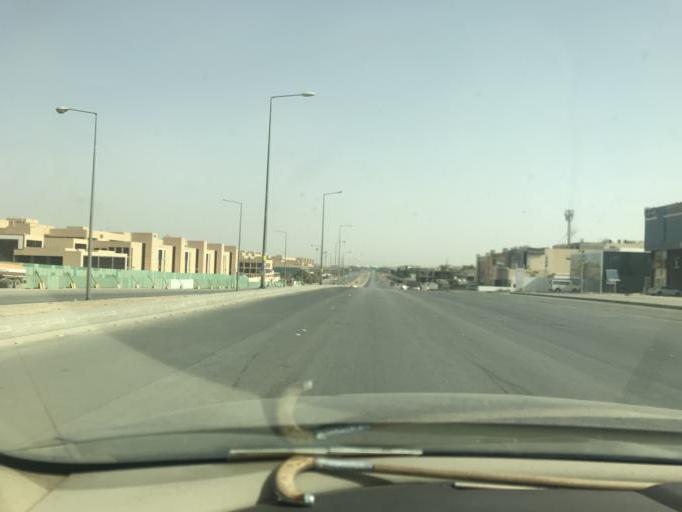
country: SA
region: Ar Riyad
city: Riyadh
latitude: 24.8164
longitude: 46.6884
